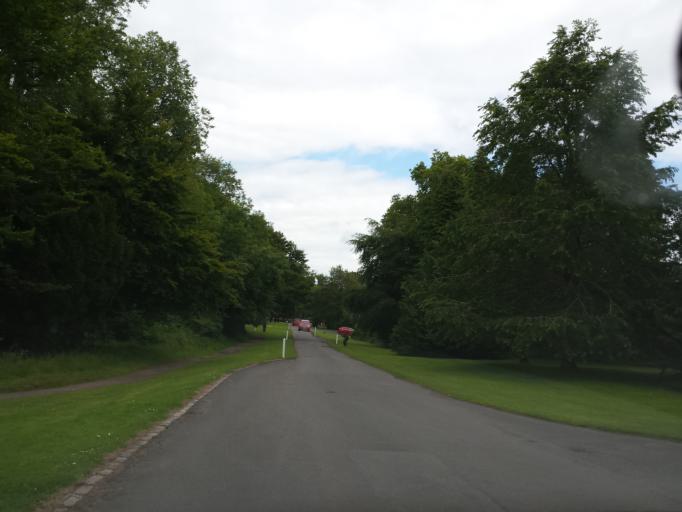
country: GB
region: Scotland
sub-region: South Ayrshire
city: Maybole
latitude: 55.3506
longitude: -4.7933
